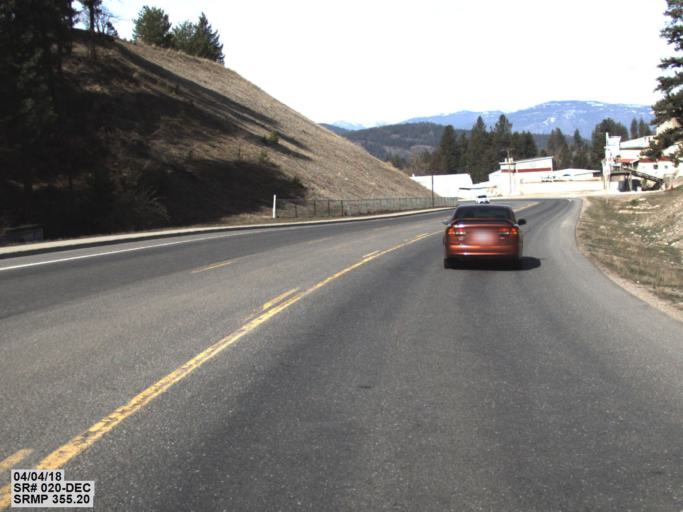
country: US
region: Washington
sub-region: Stevens County
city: Colville
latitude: 48.5469
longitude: -117.8874
